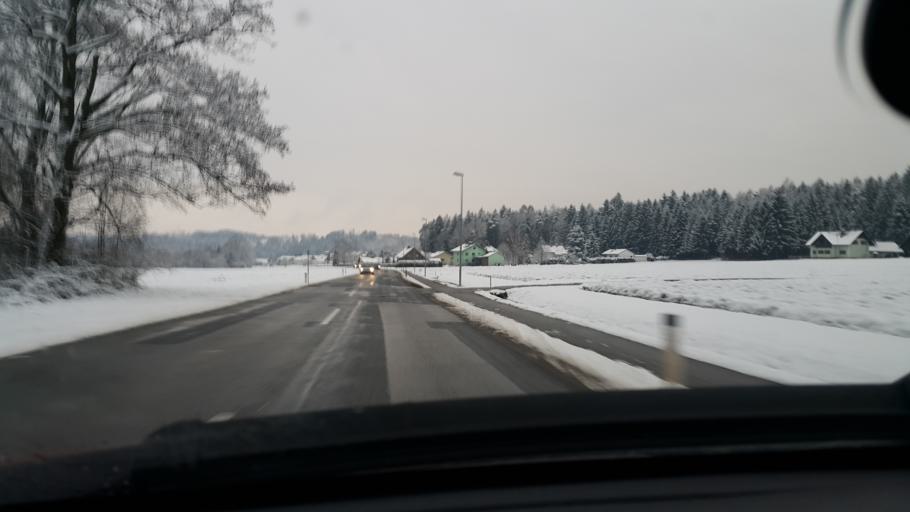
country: AT
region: Styria
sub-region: Politischer Bezirk Graz-Umgebung
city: Hitzendorf
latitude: 47.0608
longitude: 15.2933
